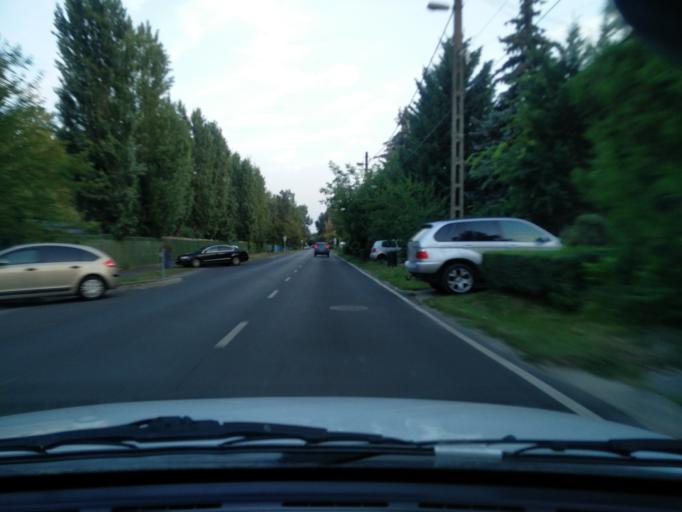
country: HU
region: Budapest
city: Budapest XXIII. keruelet
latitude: 47.4057
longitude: 19.1007
